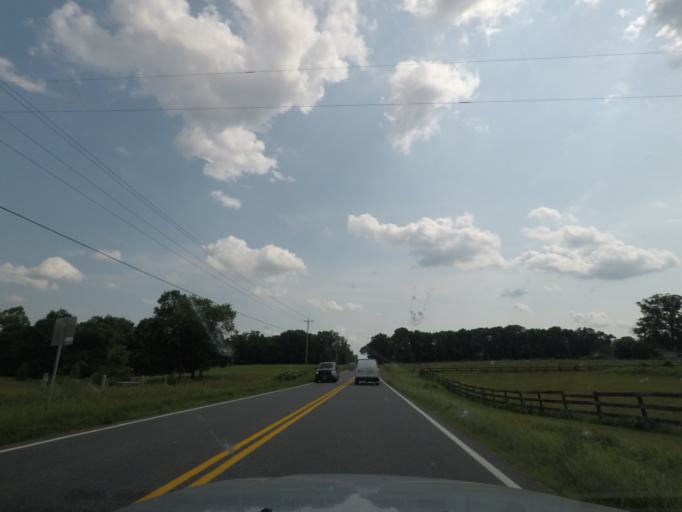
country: US
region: Virginia
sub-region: Fluvanna County
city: Palmyra
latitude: 37.9323
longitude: -78.2482
